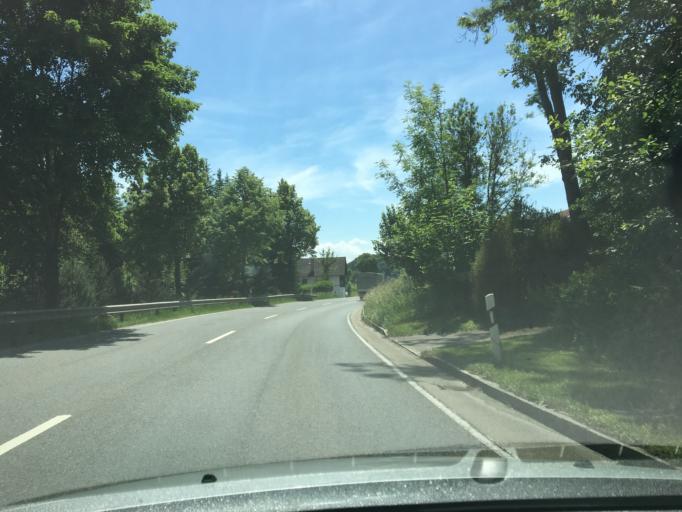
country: DE
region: Bavaria
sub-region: Upper Bavaria
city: Laufen
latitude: 47.9245
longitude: 12.9393
